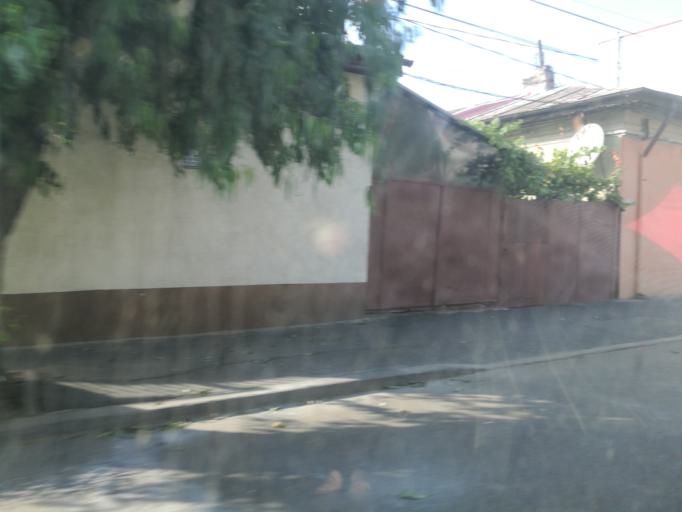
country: RO
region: Ilfov
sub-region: Comuna Chiajna
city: Rosu
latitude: 44.4718
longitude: 26.0527
